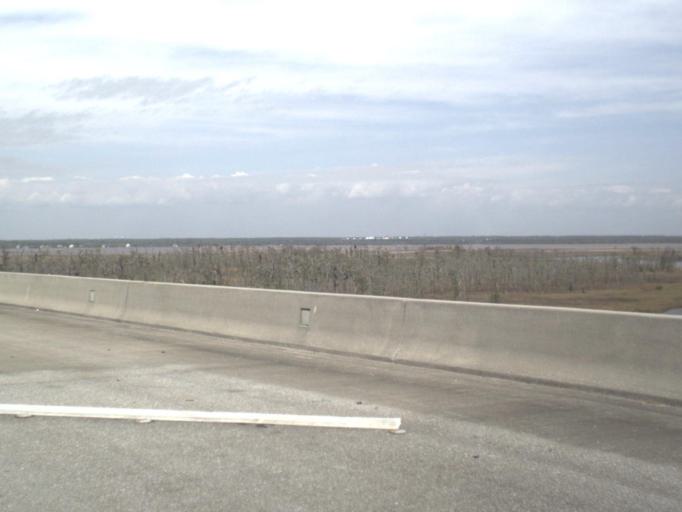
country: US
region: Florida
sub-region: Escambia County
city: Ferry Pass
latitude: 30.5486
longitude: -87.1951
